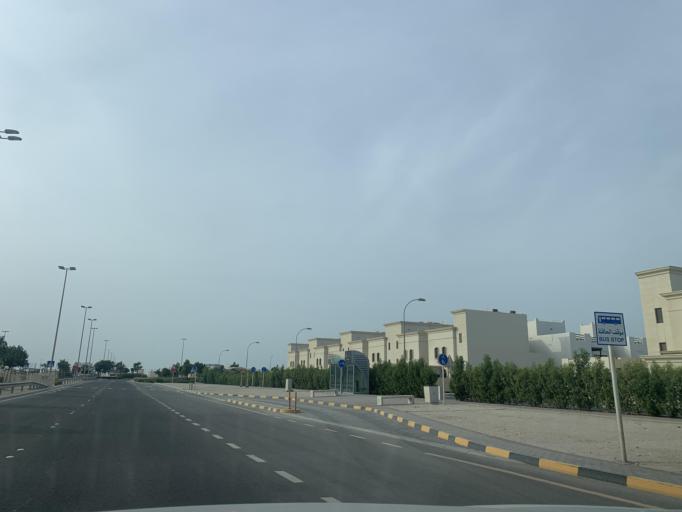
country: BH
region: Muharraq
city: Al Muharraq
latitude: 26.3168
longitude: 50.6260
